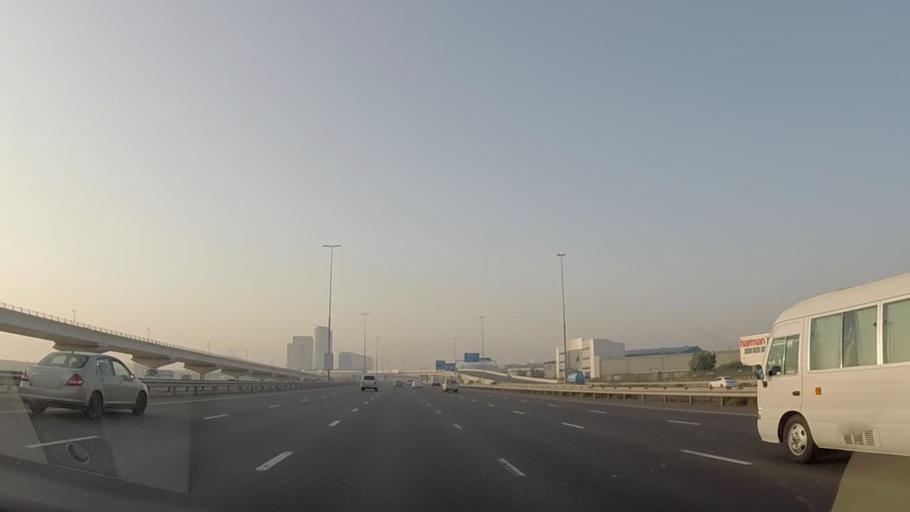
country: AE
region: Dubai
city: Dubai
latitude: 24.9955
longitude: 55.0941
